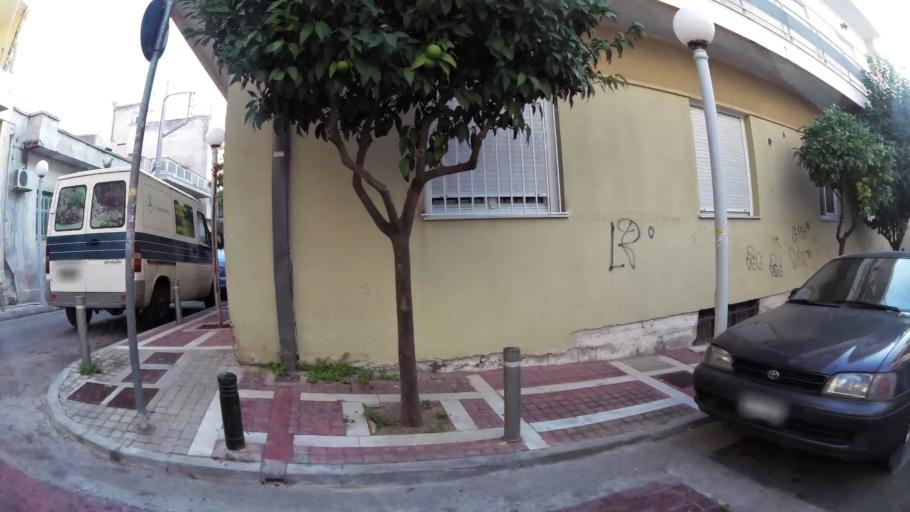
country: GR
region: Attica
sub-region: Nomarchia Athinas
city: Dhafni
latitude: 37.9484
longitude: 23.7336
